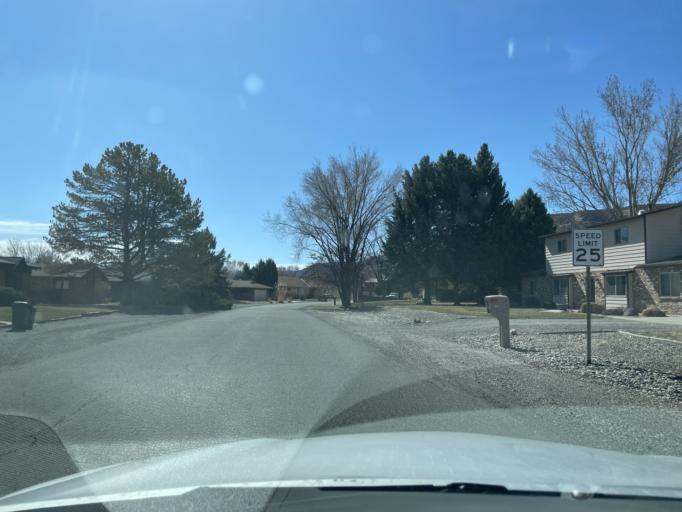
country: US
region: Colorado
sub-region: Mesa County
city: Redlands
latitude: 39.0842
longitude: -108.6721
